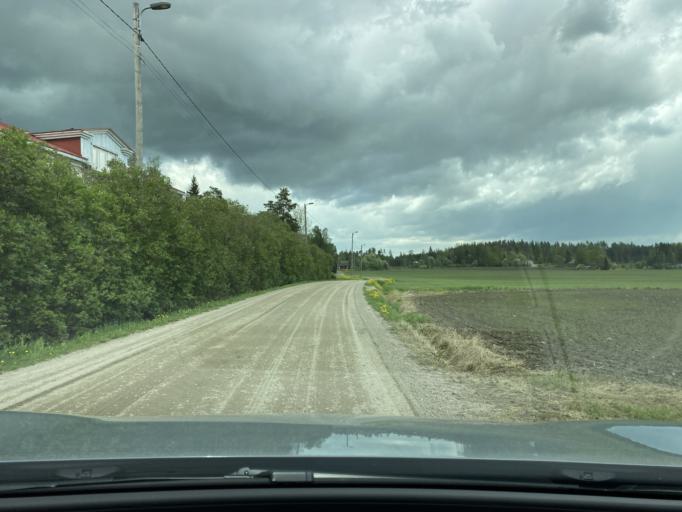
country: FI
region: Uusimaa
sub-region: Helsinki
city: Maentsaelae
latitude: 60.7587
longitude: 25.4322
